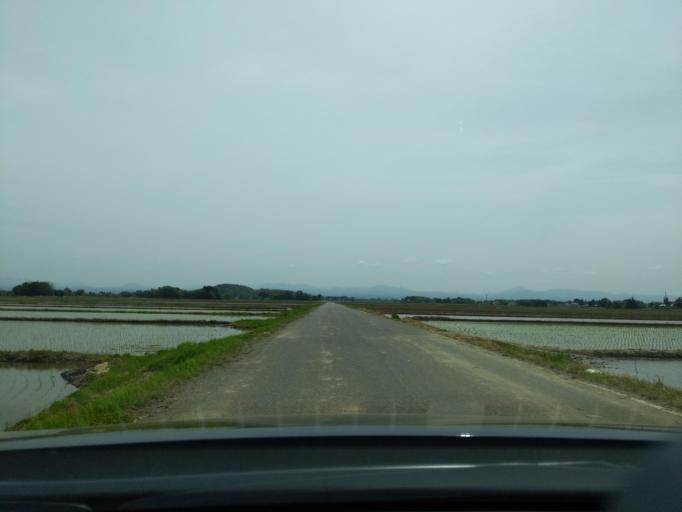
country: JP
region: Fukushima
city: Koriyama
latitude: 37.3992
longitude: 140.2744
